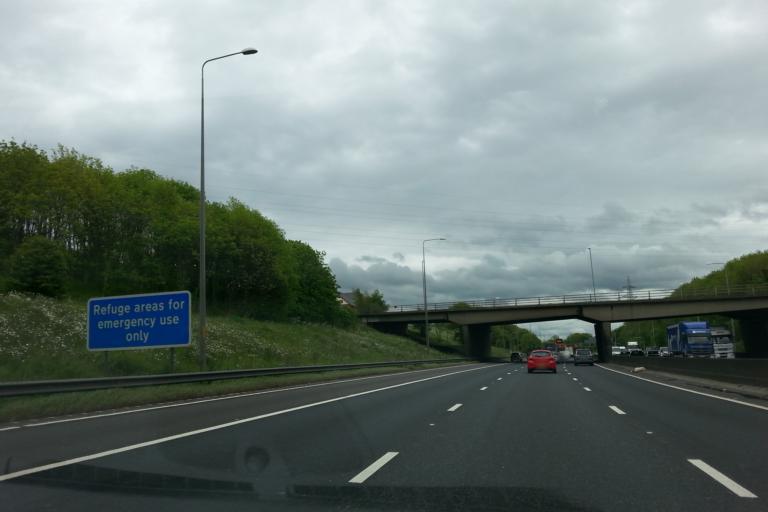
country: GB
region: England
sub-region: Kirklees
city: Cleckheaton
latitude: 53.7449
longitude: -1.7009
